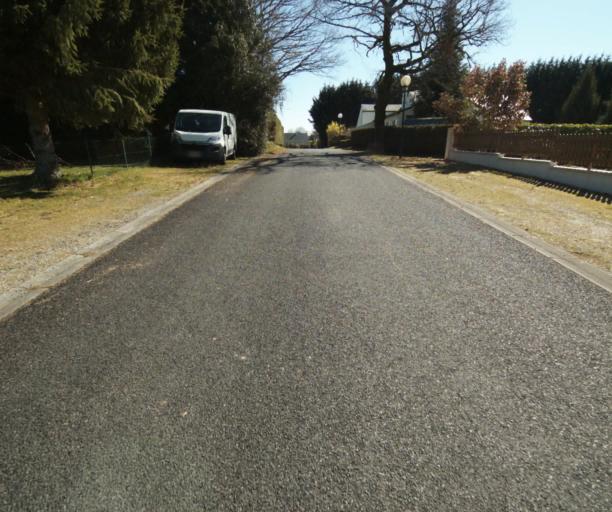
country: FR
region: Limousin
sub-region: Departement de la Correze
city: Chamboulive
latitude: 45.4268
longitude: 1.7046
